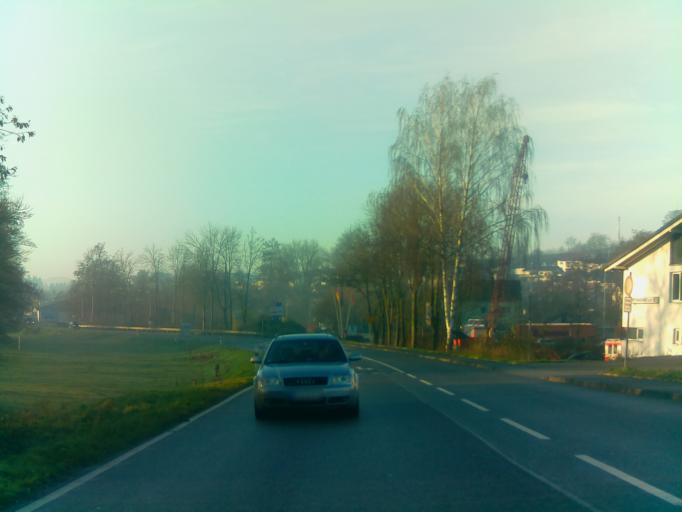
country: DE
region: Hesse
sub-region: Regierungsbezirk Darmstadt
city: Furth
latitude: 49.6593
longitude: 8.7895
